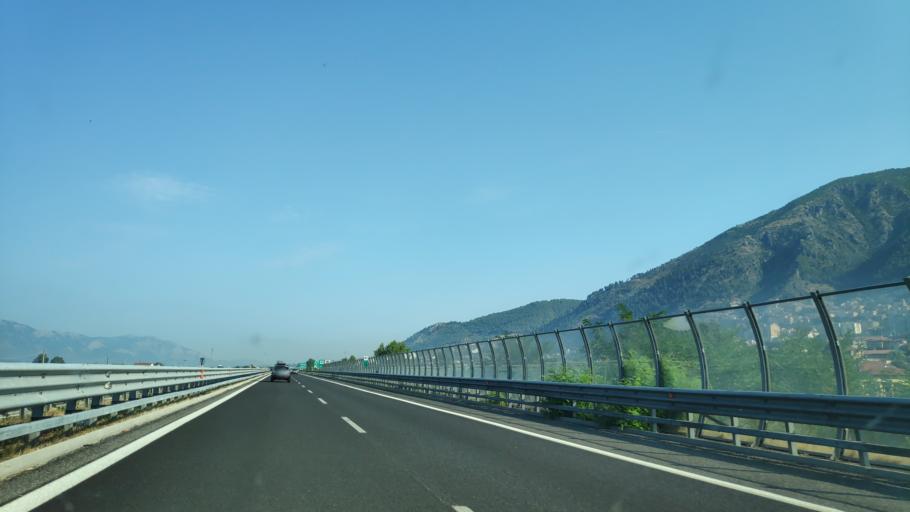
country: IT
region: Campania
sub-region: Provincia di Salerno
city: Sala Consilina
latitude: 40.3890
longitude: 15.5880
